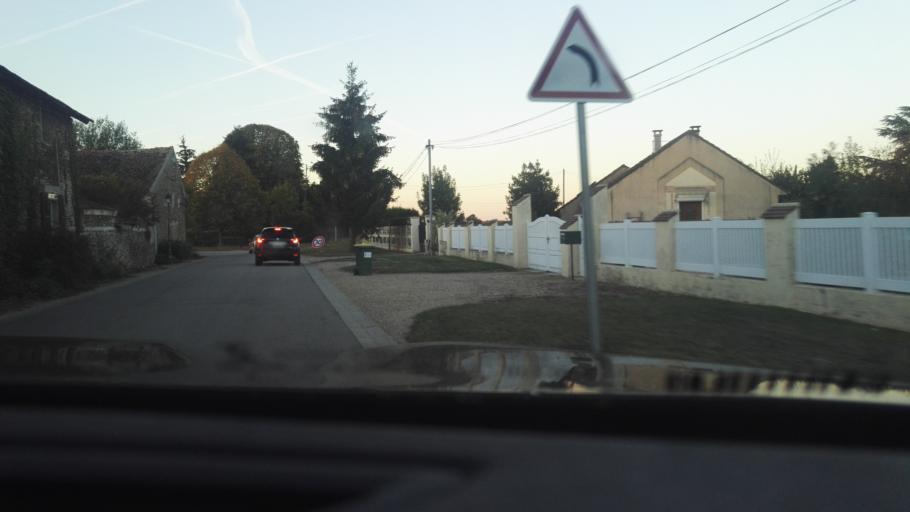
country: FR
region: Ile-de-France
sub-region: Departement des Yvelines
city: Longnes
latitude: 48.8577
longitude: 1.5897
